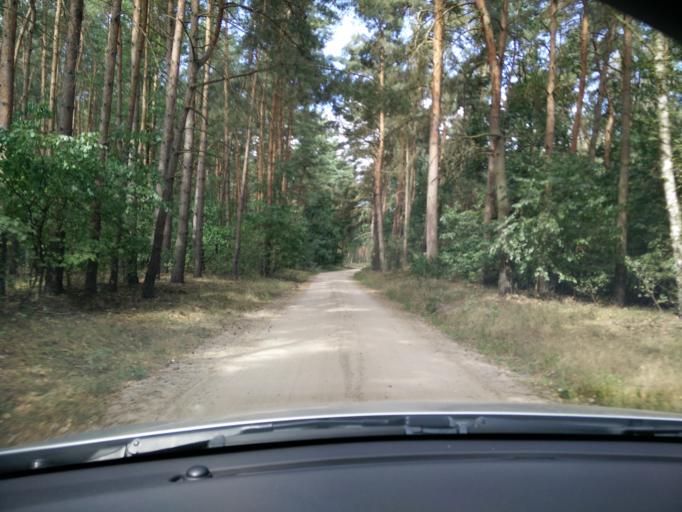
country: PL
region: Greater Poland Voivodeship
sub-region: Powiat sredzki
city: Sroda Wielkopolska
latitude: 52.2813
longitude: 17.2442
